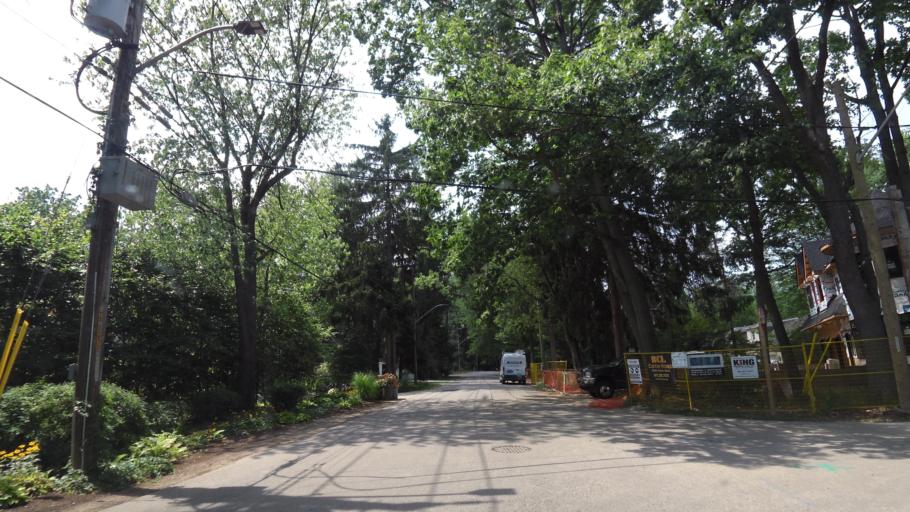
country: CA
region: Ontario
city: Mississauga
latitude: 43.5560
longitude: -79.6011
